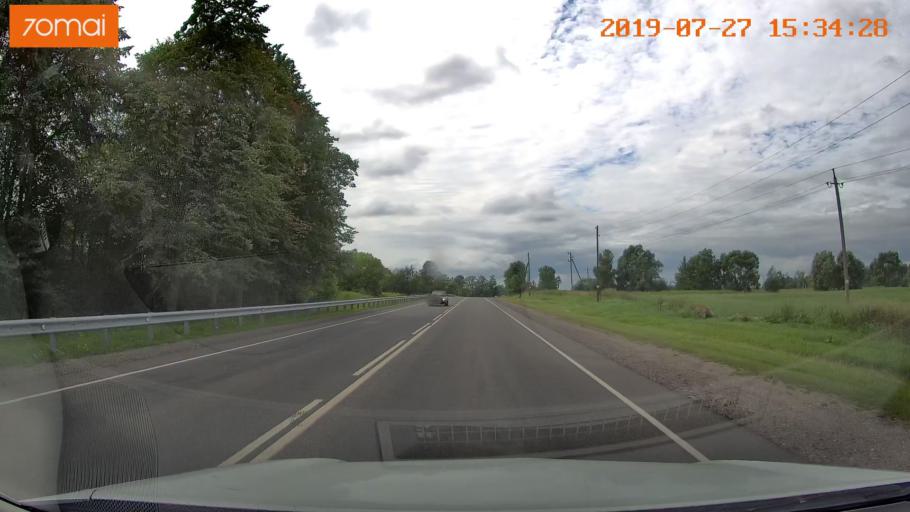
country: RU
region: Kaliningrad
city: Nesterov
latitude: 54.6119
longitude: 22.4234
